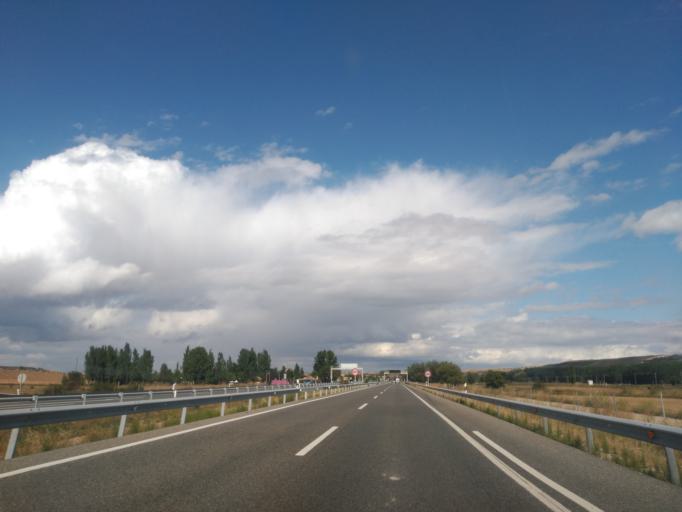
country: ES
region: Castille and Leon
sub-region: Provincia de Burgos
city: Frandovinez
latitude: 42.2899
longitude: -3.8546
